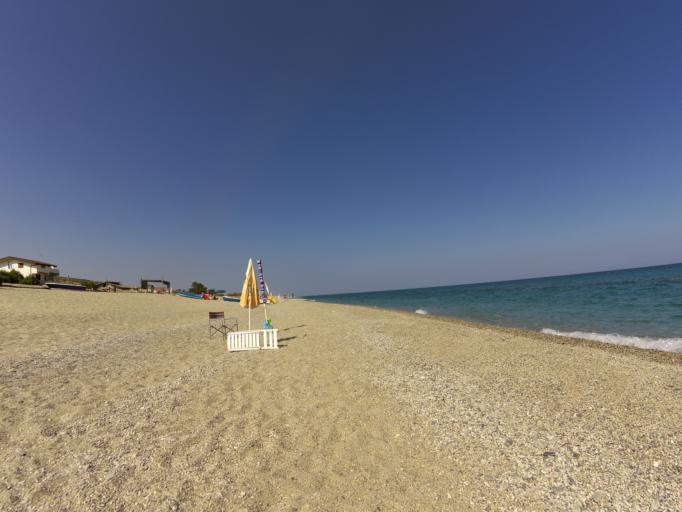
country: IT
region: Calabria
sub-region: Provincia di Reggio Calabria
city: Riace Marina
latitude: 38.3991
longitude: 16.5424
